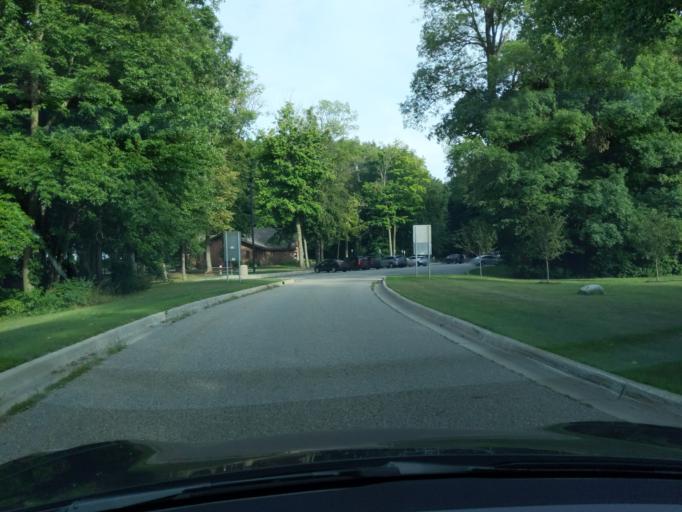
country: US
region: Michigan
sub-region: Ionia County
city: Saranac
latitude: 42.8783
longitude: -85.1609
